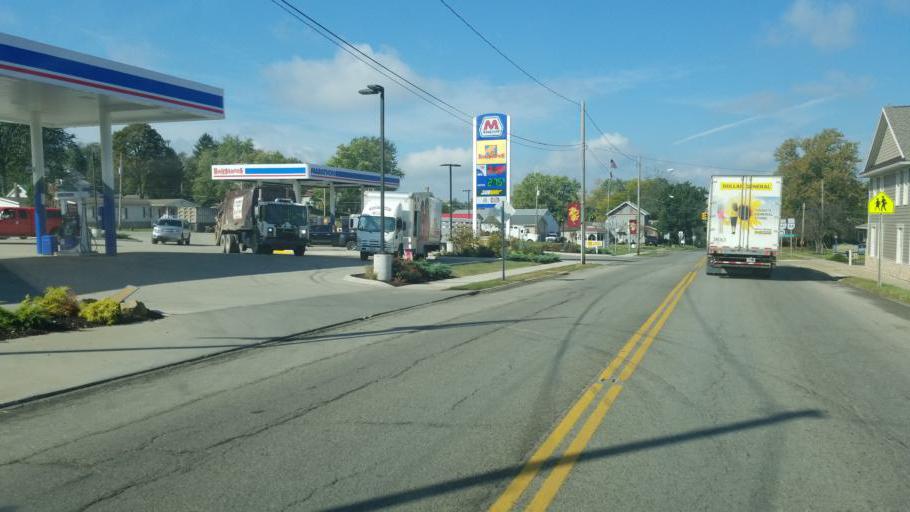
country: US
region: Ohio
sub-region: Stark County
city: Brewster
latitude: 40.6942
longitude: -81.7016
